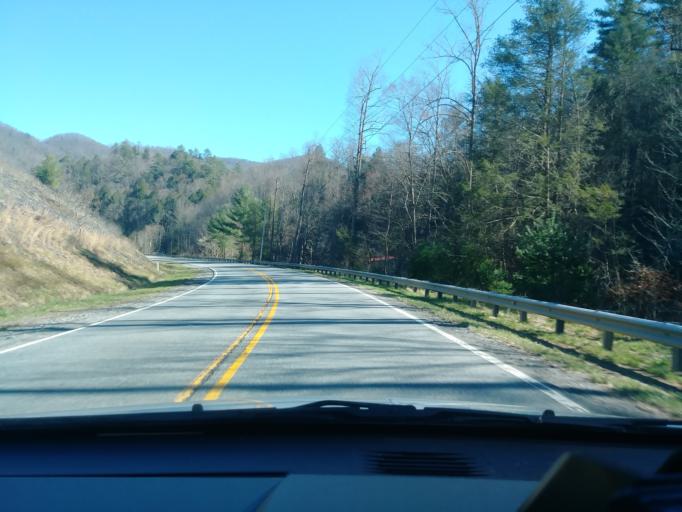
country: US
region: North Carolina
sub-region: Madison County
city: Marshall
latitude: 35.9149
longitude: -82.7648
